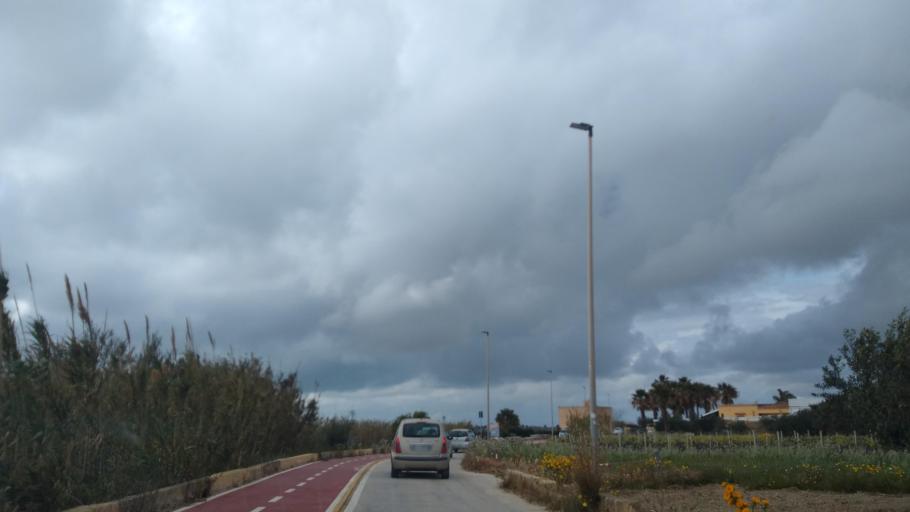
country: IT
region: Sicily
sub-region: Trapani
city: Marsala
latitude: 37.8611
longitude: 12.4852
